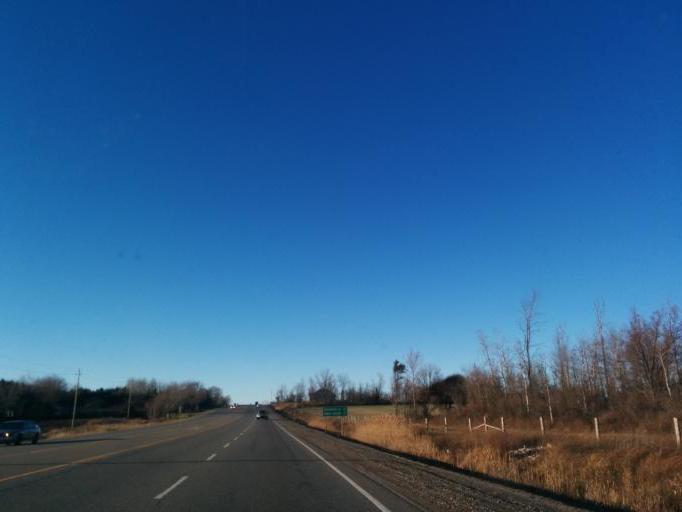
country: CA
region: Ontario
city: Orangeville
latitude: 43.8664
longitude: -80.0040
